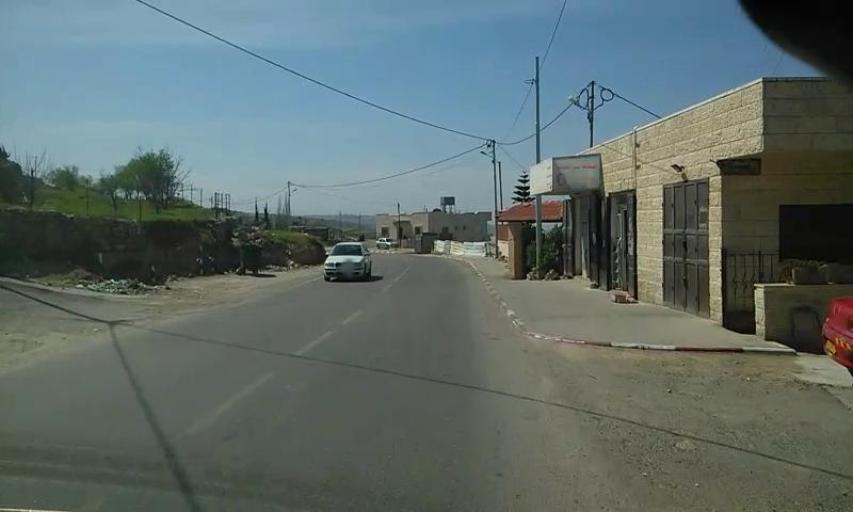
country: PS
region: West Bank
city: Husan
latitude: 31.7072
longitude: 35.1464
